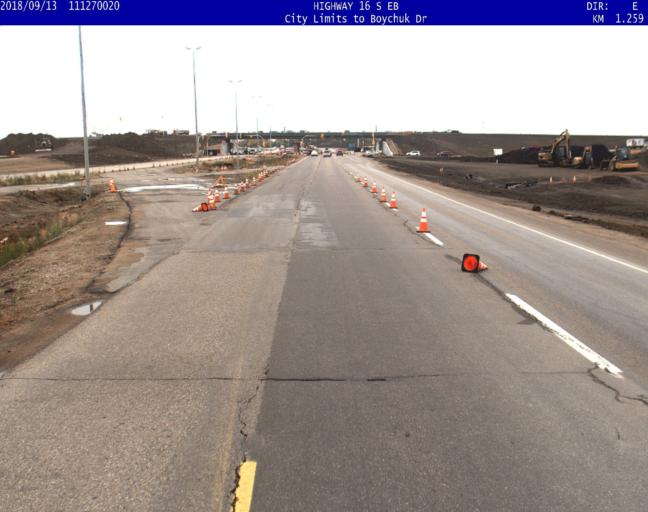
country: CA
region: Saskatchewan
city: Saskatoon
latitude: 52.0884
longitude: -106.5796
